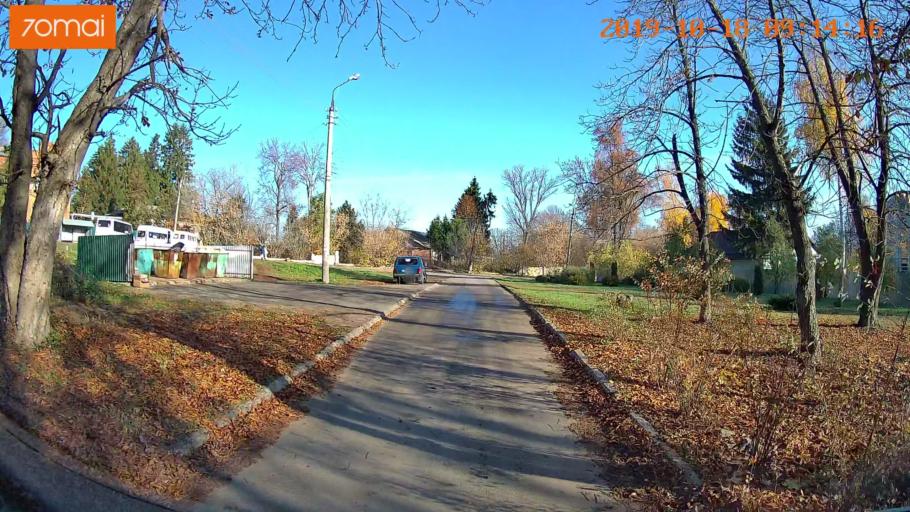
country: RU
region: Tula
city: Yefremov
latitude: 53.1321
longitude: 38.1122
